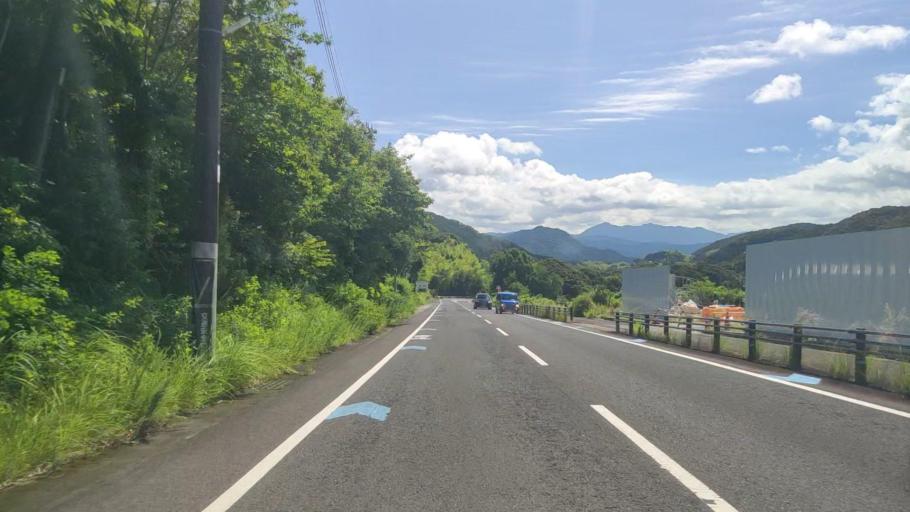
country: JP
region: Wakayama
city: Shingu
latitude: 33.7439
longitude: 136.0090
